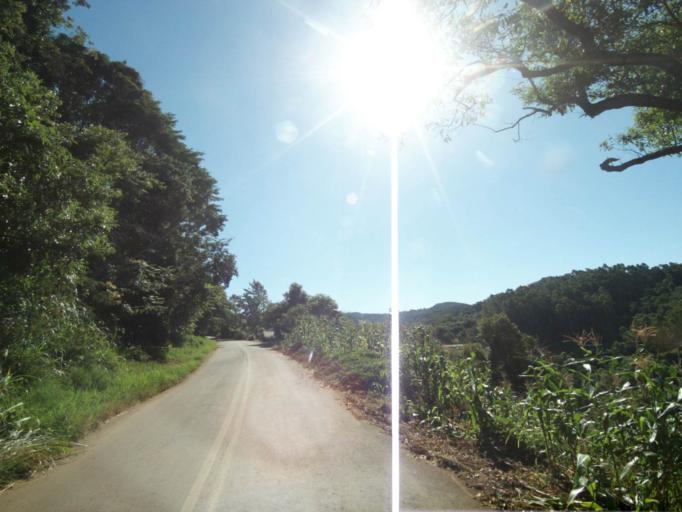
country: BR
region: Parana
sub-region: Ampere
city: Ampere
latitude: -26.1711
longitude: -53.3687
